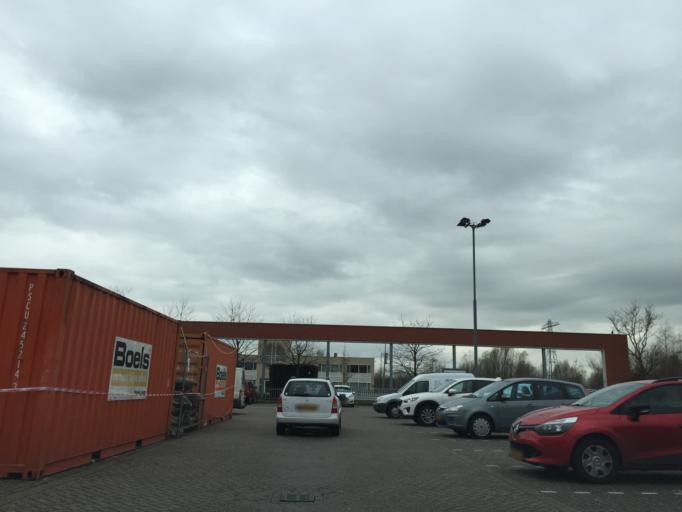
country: NL
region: South Holland
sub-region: Gemeente Schiedam
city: Schiedam
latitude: 51.9367
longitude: 4.3990
